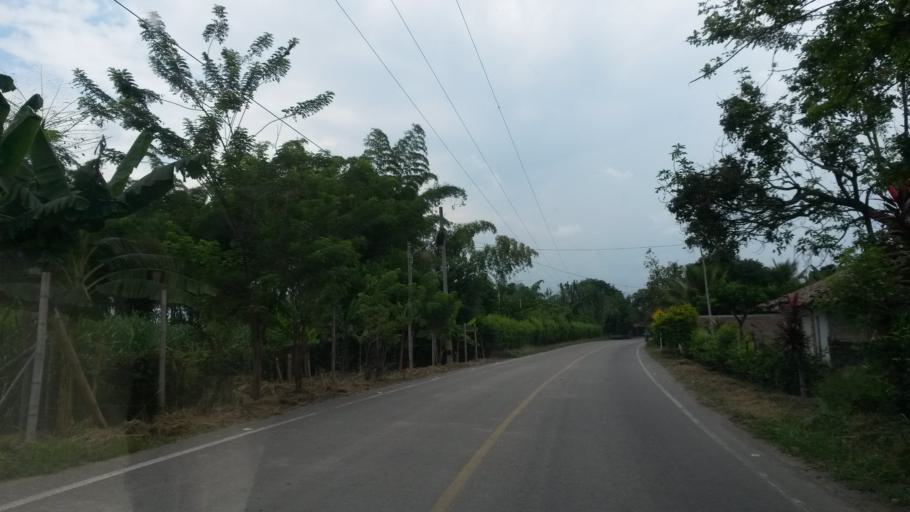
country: CO
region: Cauca
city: Padilla
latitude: 3.2309
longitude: -76.3248
